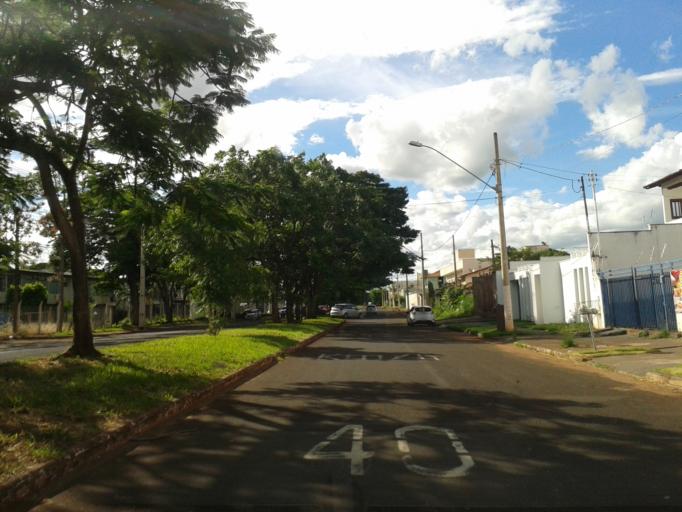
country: BR
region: Minas Gerais
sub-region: Ituiutaba
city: Ituiutaba
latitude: -18.9726
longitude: -49.4457
